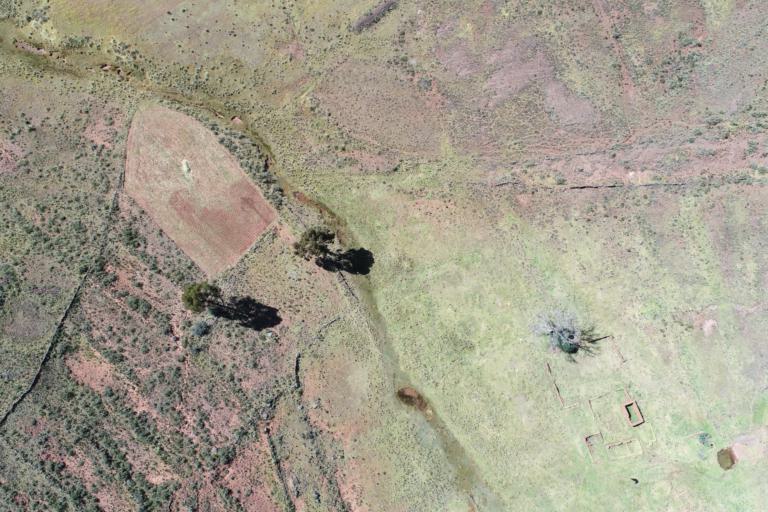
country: BO
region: La Paz
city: Tiahuanaco
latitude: -16.6072
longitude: -68.7743
